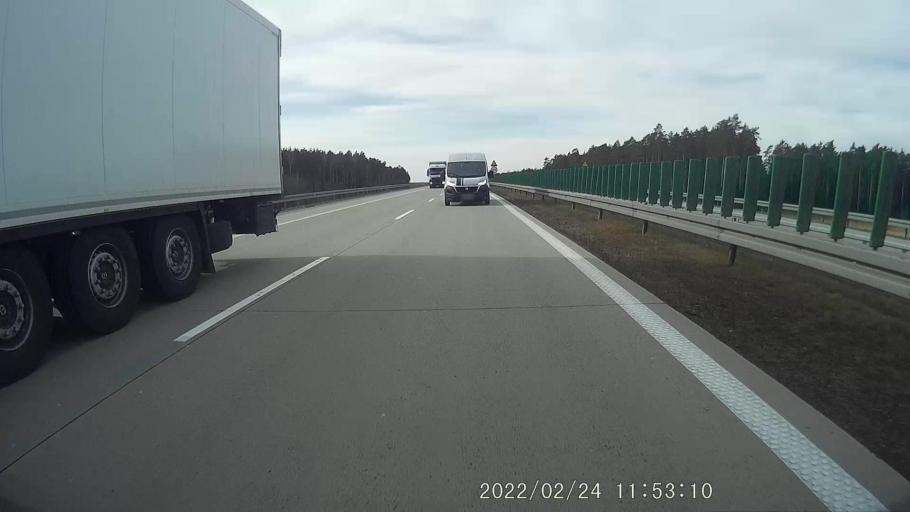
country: PL
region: Lower Silesian Voivodeship
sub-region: Powiat polkowicki
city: Radwanice
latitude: 51.6272
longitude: 15.9764
